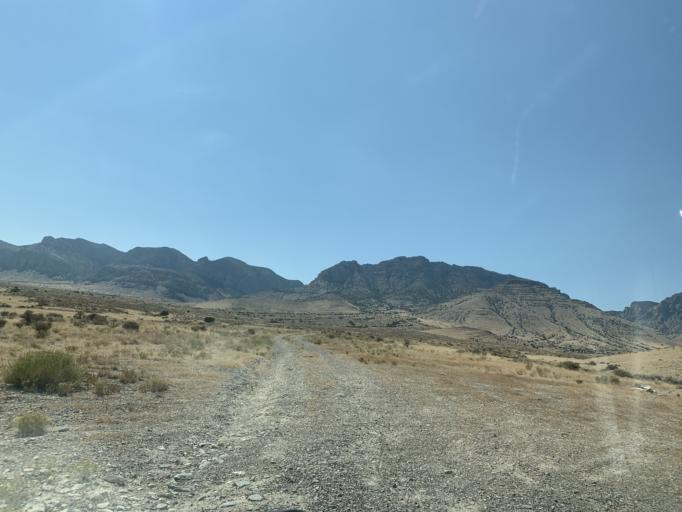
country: US
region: Utah
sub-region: Beaver County
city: Milford
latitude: 38.9754
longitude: -113.4522
